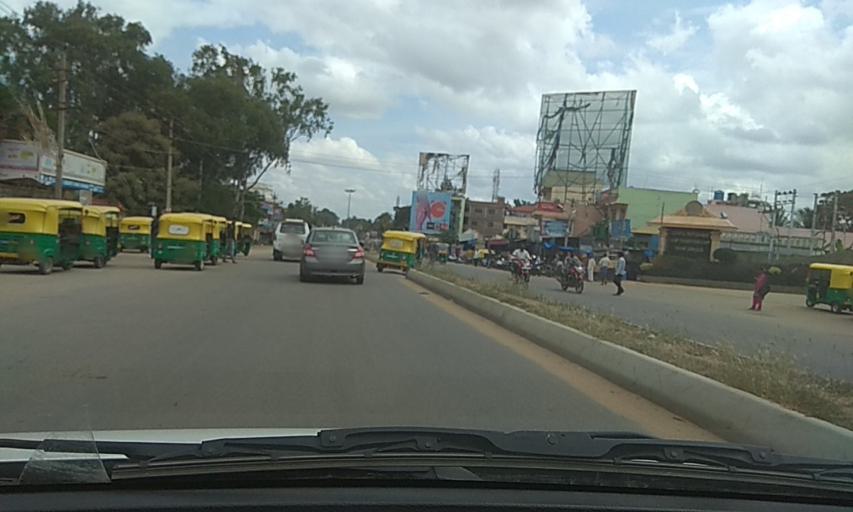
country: IN
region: Karnataka
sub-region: Tumkur
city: Tumkur
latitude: 13.3764
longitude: 77.0991
